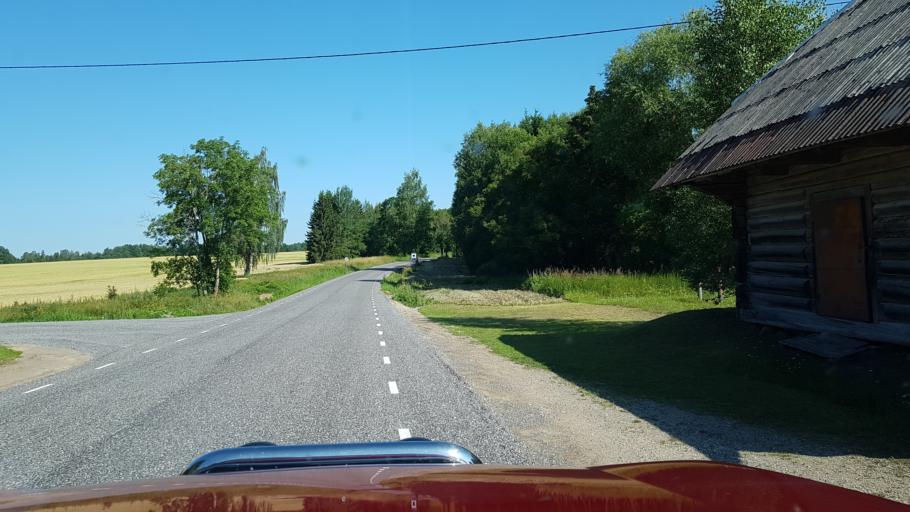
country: EE
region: Polvamaa
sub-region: Polva linn
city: Polva
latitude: 58.0019
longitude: 26.9280
